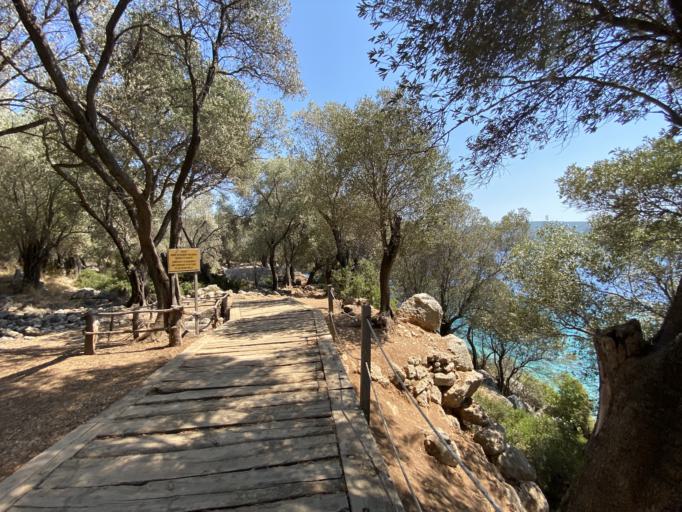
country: TR
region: Mugla
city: Yerkesik
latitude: 36.9915
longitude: 28.2074
